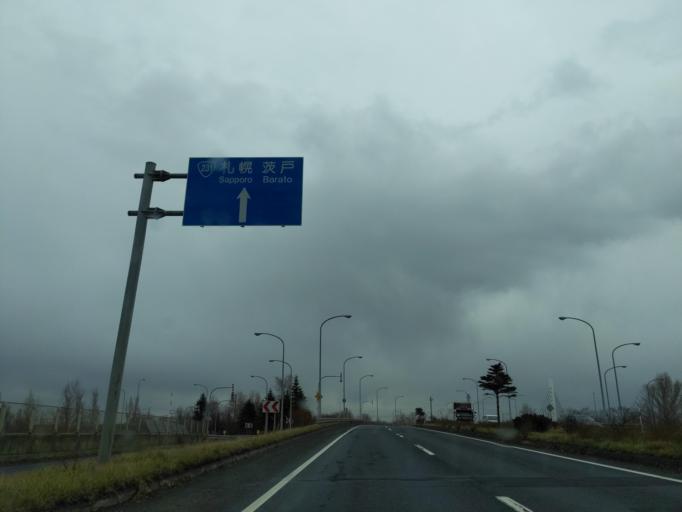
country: JP
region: Hokkaido
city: Ishikari
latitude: 43.1844
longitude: 141.3206
